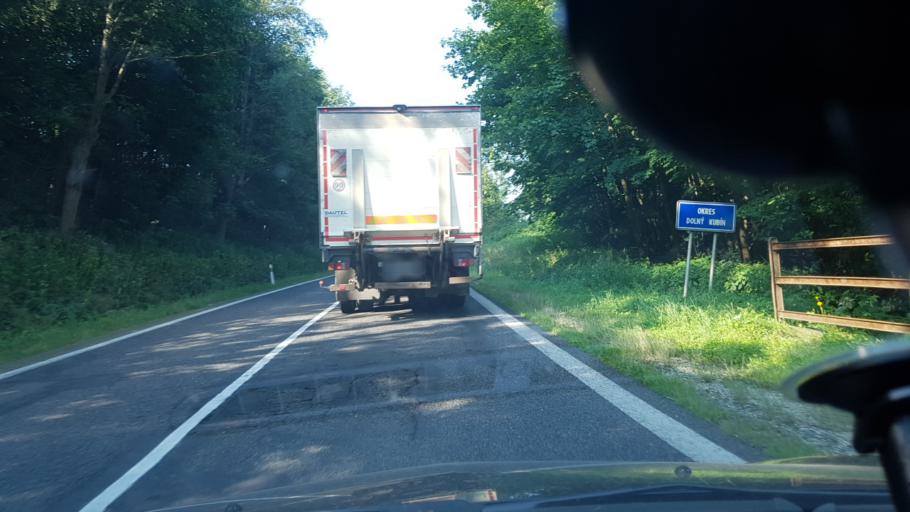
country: SK
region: Zilinsky
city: Tvrdosin
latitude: 49.2883
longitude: 19.4928
